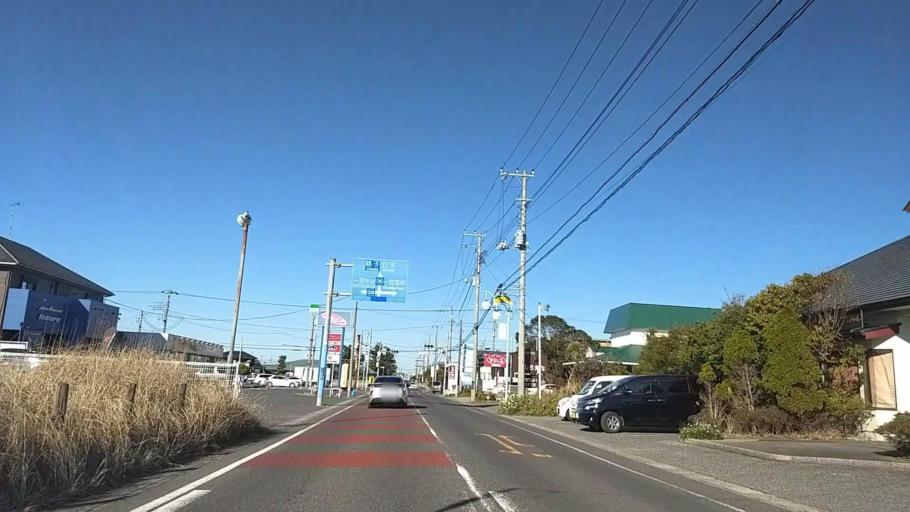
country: JP
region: Chiba
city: Mobara
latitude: 35.3724
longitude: 140.3876
